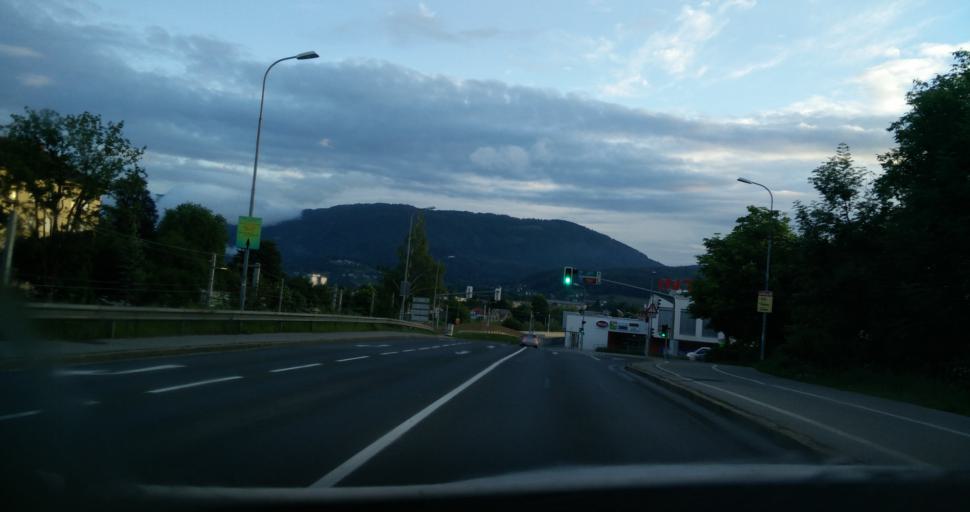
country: AT
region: Carinthia
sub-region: Villach Stadt
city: Villach
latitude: 46.6132
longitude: 13.8420
